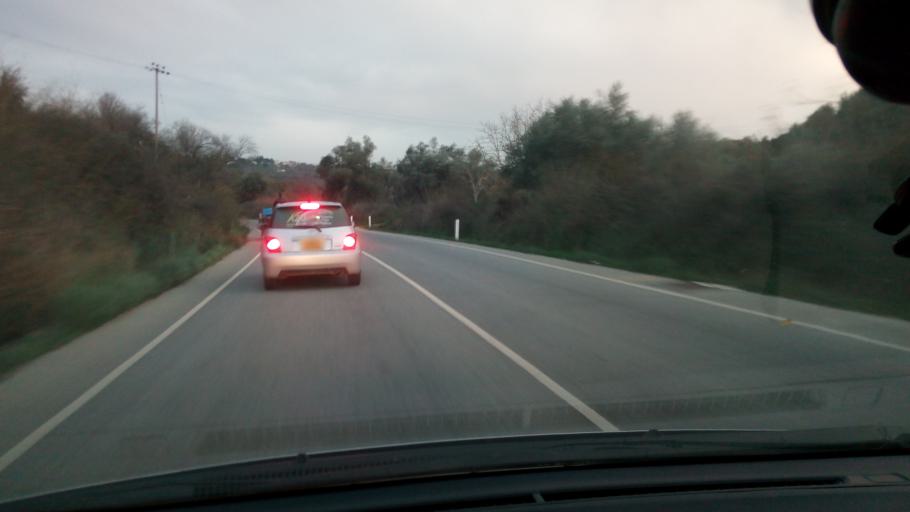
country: CY
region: Pafos
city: Pegeia
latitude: 34.9378
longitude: 32.4690
